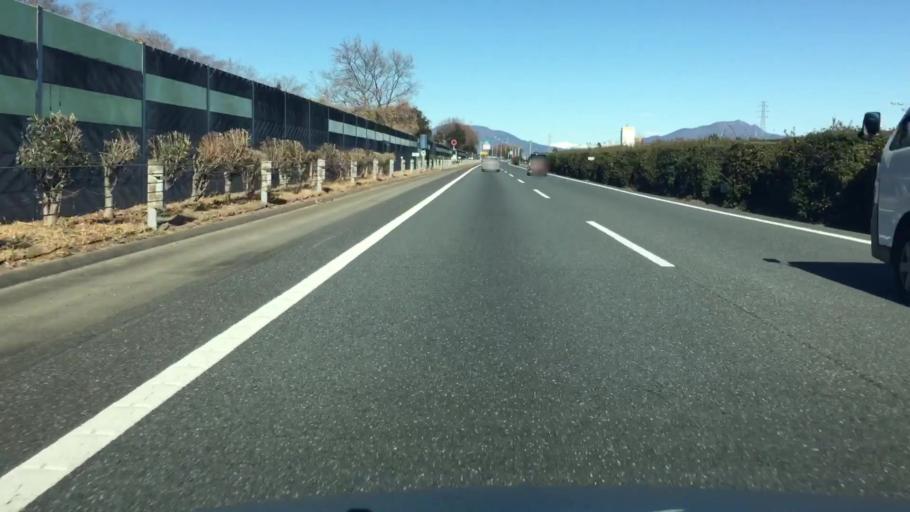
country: JP
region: Gunma
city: Kanekomachi
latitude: 36.4215
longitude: 139.0183
